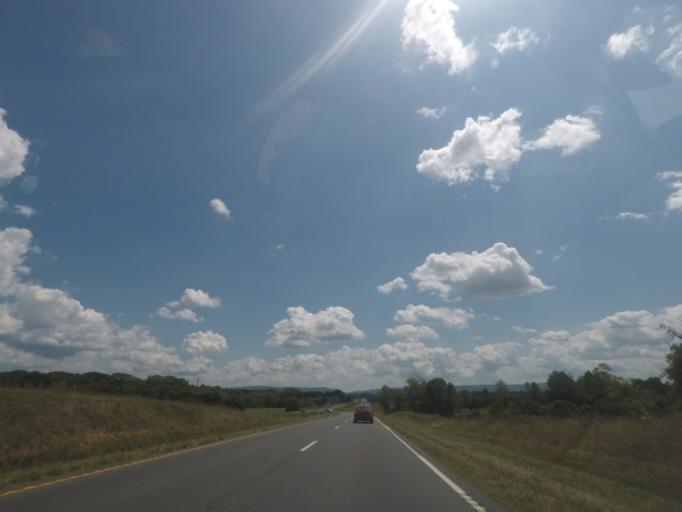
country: US
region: Virginia
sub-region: Warren County
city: Shenandoah Farms
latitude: 39.0859
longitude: -78.0890
